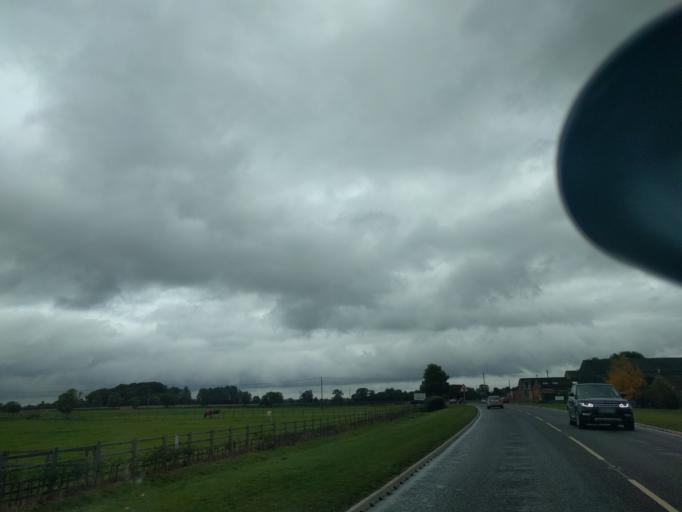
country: GB
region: England
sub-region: North Yorkshire
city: Bedale
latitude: 54.3120
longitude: -1.5403
